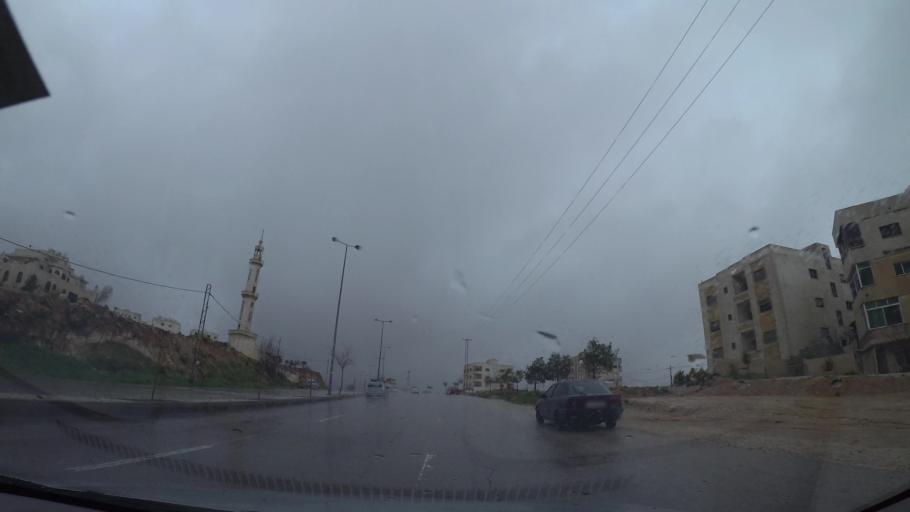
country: JO
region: Amman
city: Al Jubayhah
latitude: 32.0368
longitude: 35.8925
